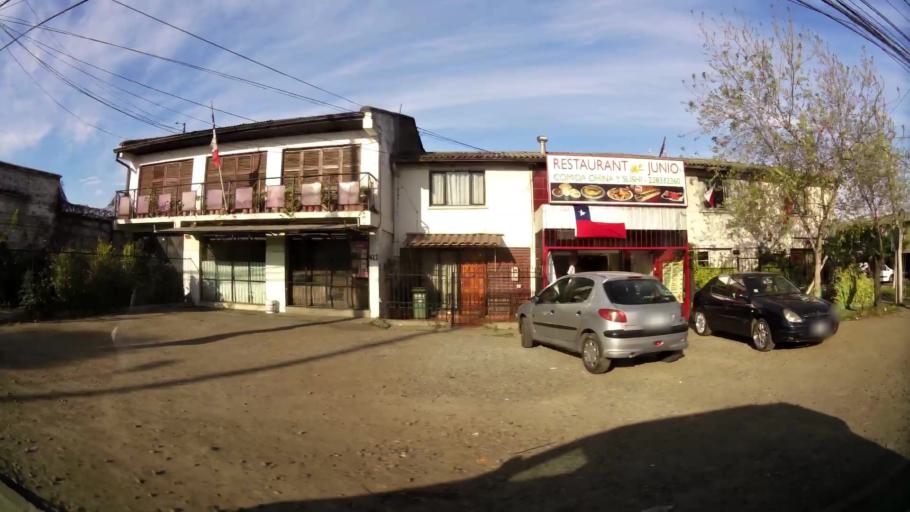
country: CL
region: Santiago Metropolitan
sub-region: Provincia de Santiago
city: Lo Prado
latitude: -33.4485
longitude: -70.7071
